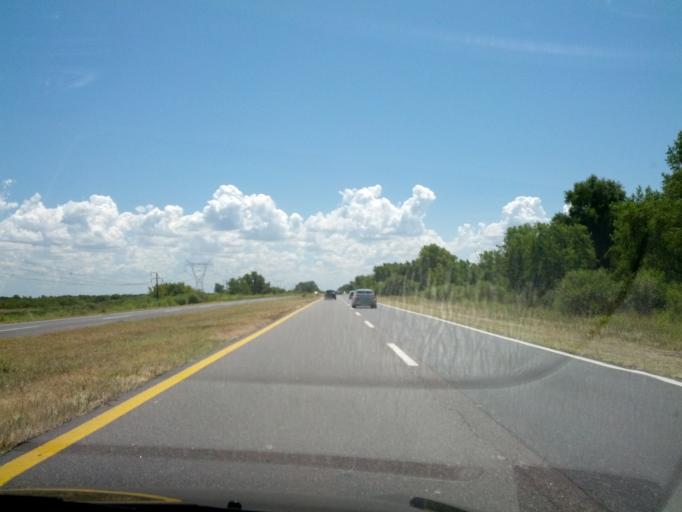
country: AR
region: Entre Rios
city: Villa Paranacito
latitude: -33.7142
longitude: -58.8496
